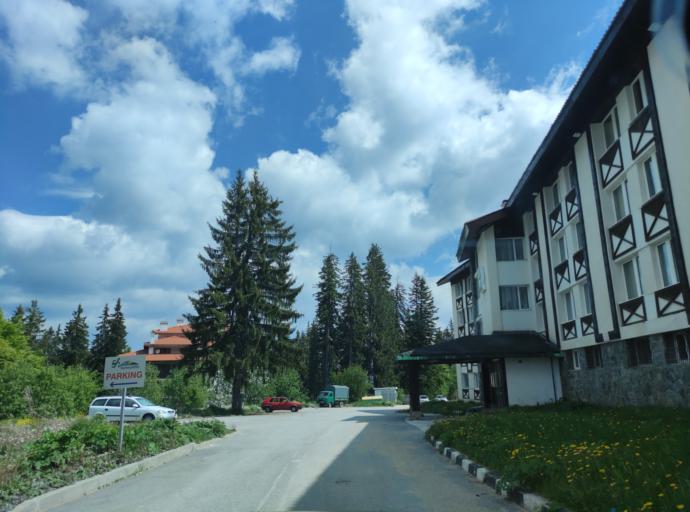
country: BG
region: Smolyan
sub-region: Obshtina Smolyan
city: Smolyan
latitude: 41.6478
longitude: 24.6963
